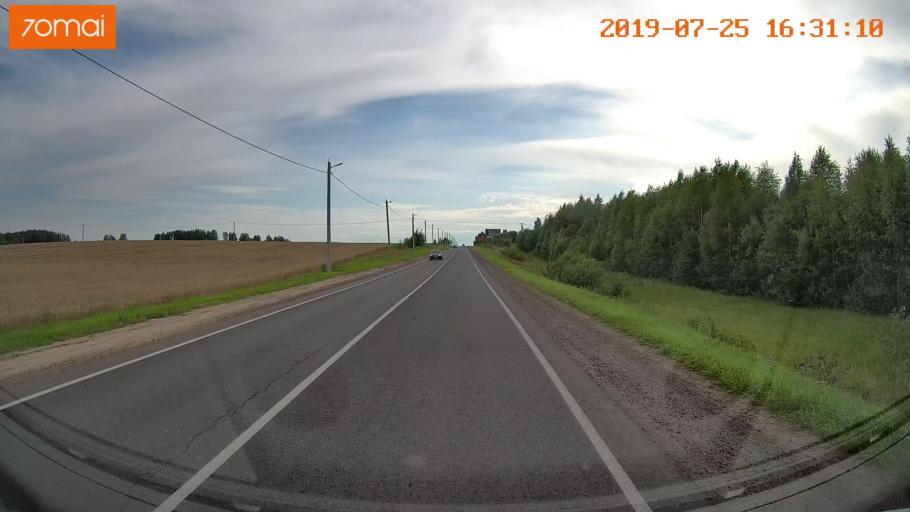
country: RU
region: Ivanovo
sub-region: Privolzhskiy Rayon
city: Ples
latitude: 57.4449
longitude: 41.4895
